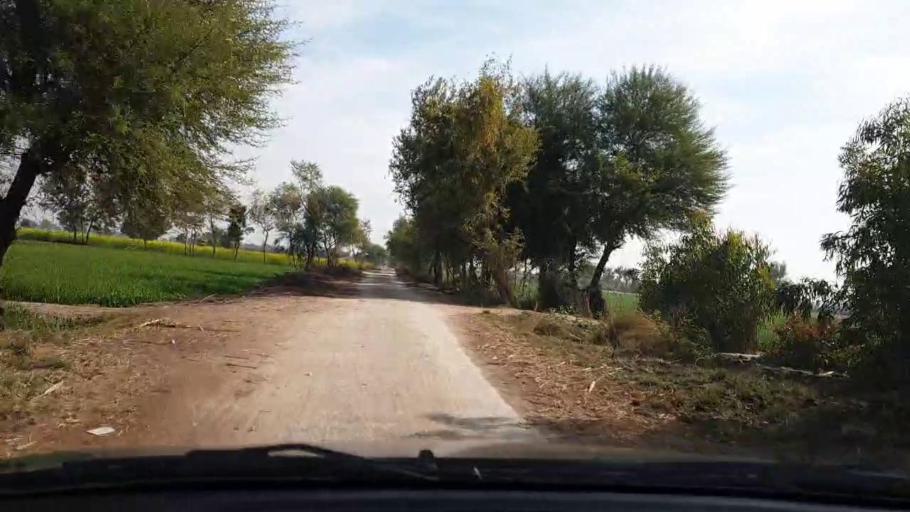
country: PK
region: Sindh
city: Jam Sahib
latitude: 26.2598
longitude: 68.7029
